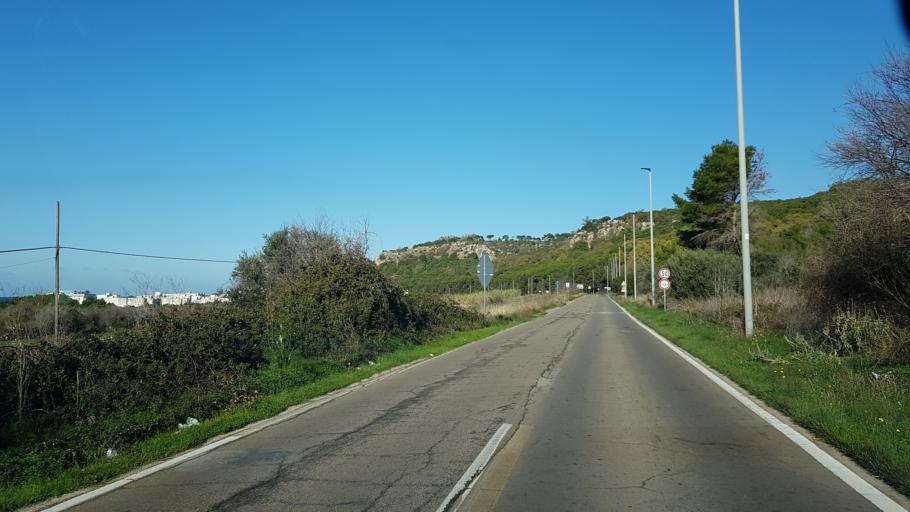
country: IT
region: Apulia
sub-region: Provincia di Lecce
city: Nardo
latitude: 40.1042
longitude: 18.0190
